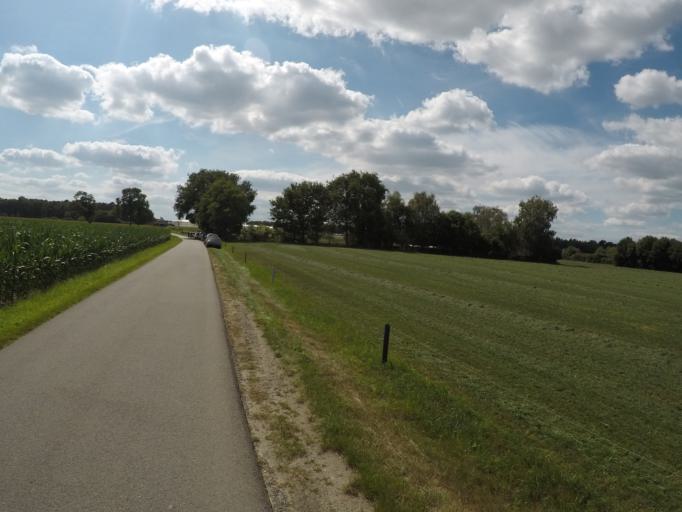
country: BE
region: Flanders
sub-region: Provincie Antwerpen
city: Herenthout
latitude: 51.1342
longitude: 4.7372
